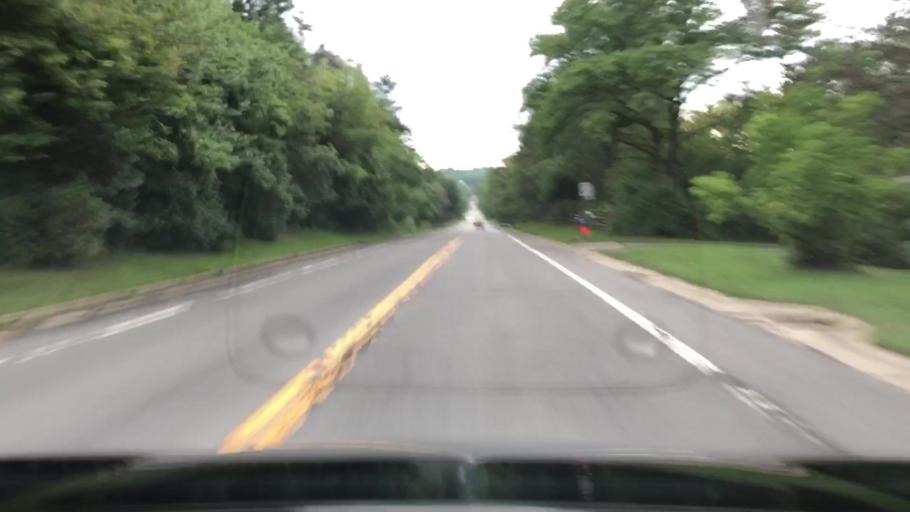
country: US
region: New York
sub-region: Erie County
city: Orchard Park
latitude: 42.7521
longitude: -78.7098
